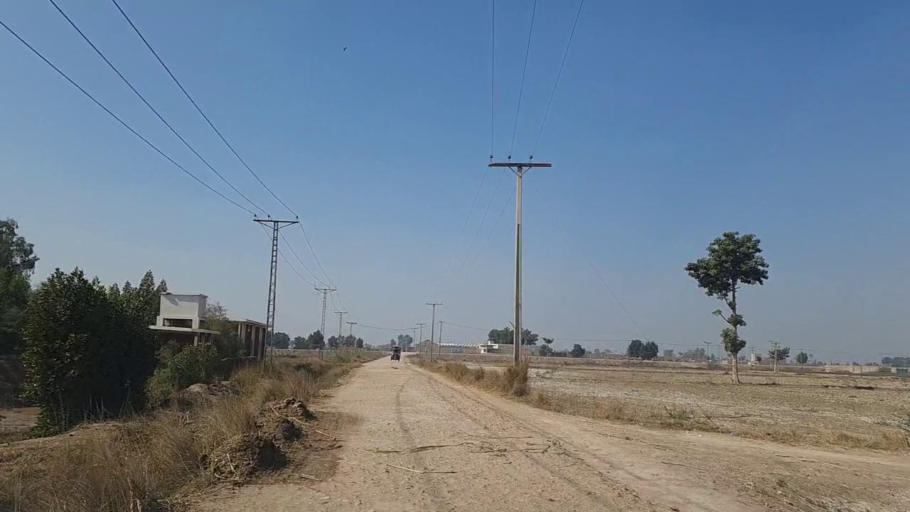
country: PK
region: Sindh
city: Daur
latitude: 26.4526
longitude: 68.3096
